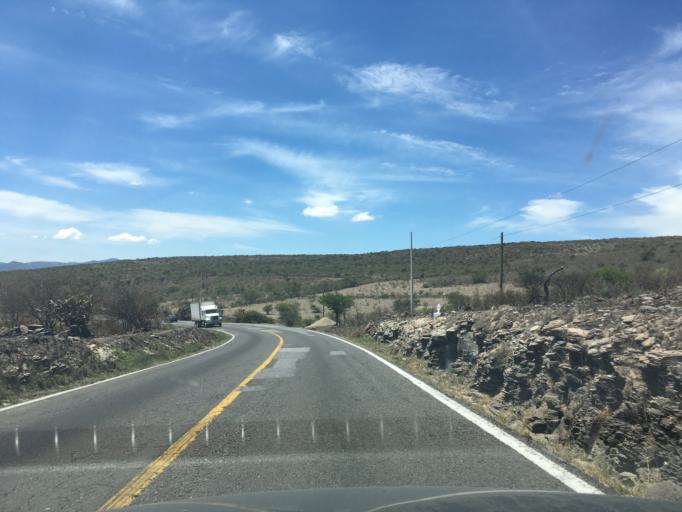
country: MX
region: Hidalgo
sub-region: Alfajayucan
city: Santa Maria Xigui
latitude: 20.4358
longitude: -99.4509
